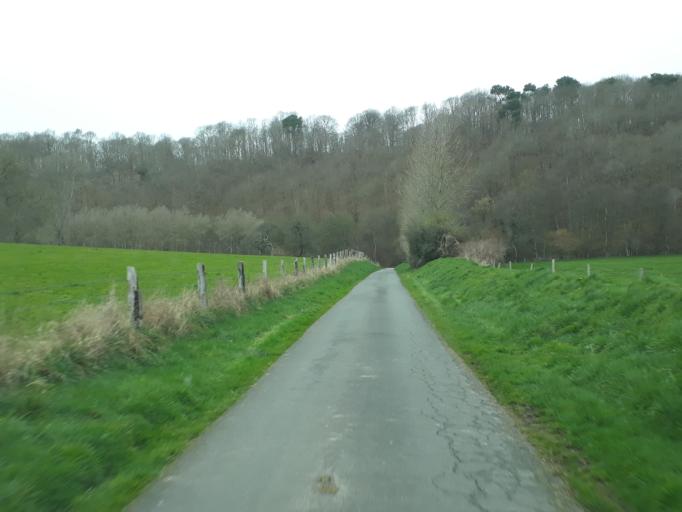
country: FR
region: Haute-Normandie
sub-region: Departement de la Seine-Maritime
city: Les Loges
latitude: 49.6746
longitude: 0.2647
